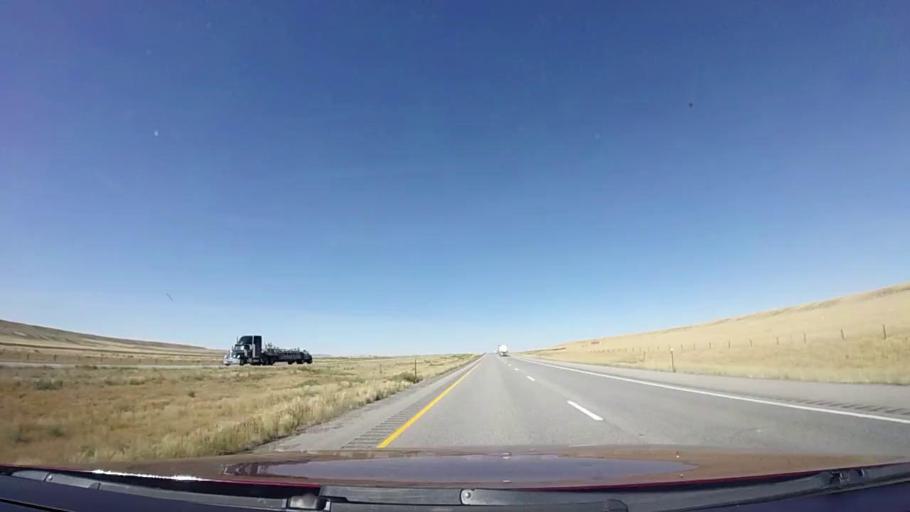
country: US
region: Wyoming
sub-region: Carbon County
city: Rawlins
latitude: 41.6567
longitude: -108.0975
